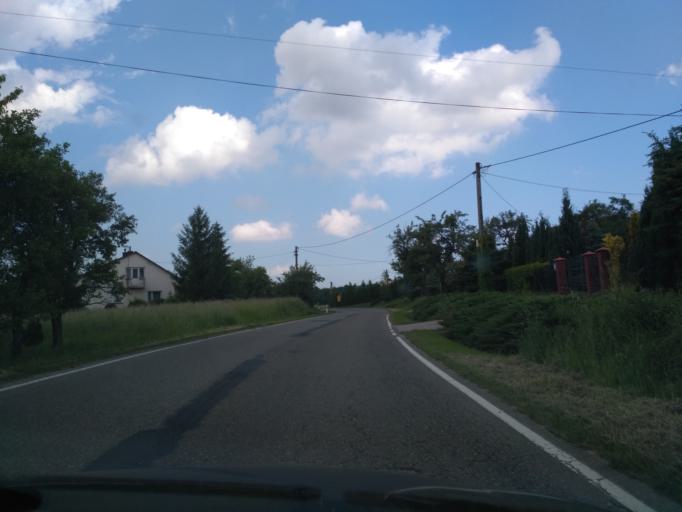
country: PL
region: Subcarpathian Voivodeship
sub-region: Powiat lancucki
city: Handzlowka
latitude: 49.9718
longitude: 22.1912
